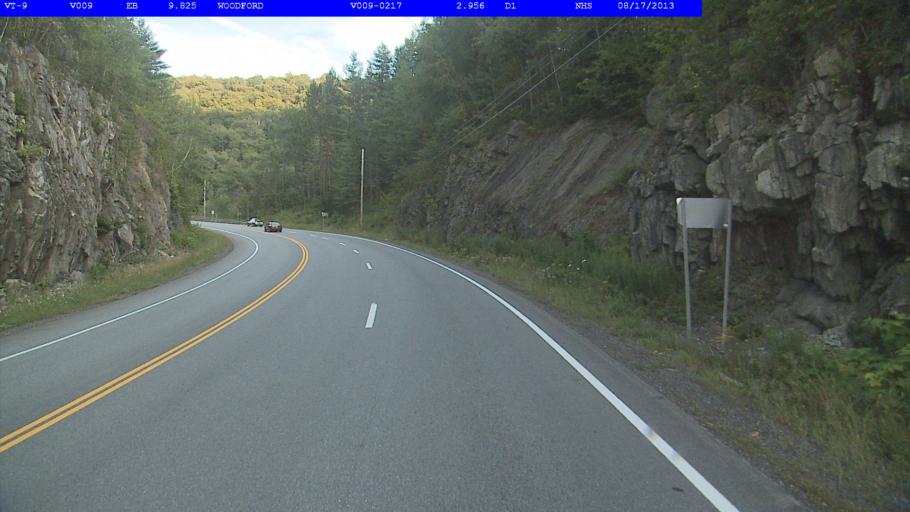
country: US
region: Vermont
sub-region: Bennington County
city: Bennington
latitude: 42.8787
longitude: -73.1167
